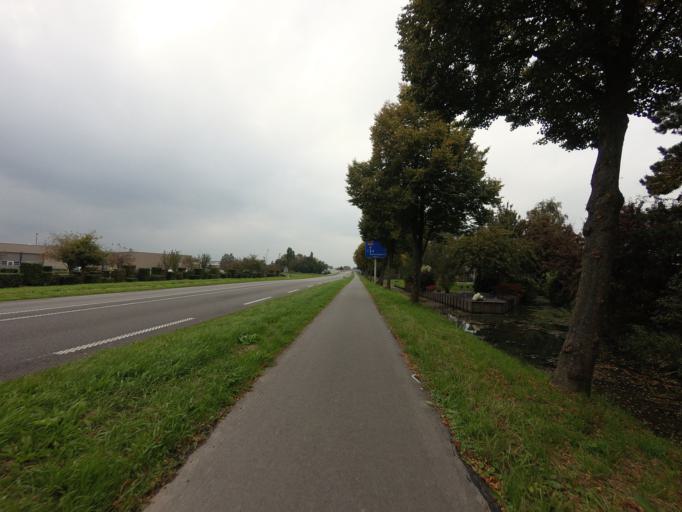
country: NL
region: South Holland
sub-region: Gemeente Schoonhoven
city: Schoonhoven
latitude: 51.9372
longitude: 4.8586
